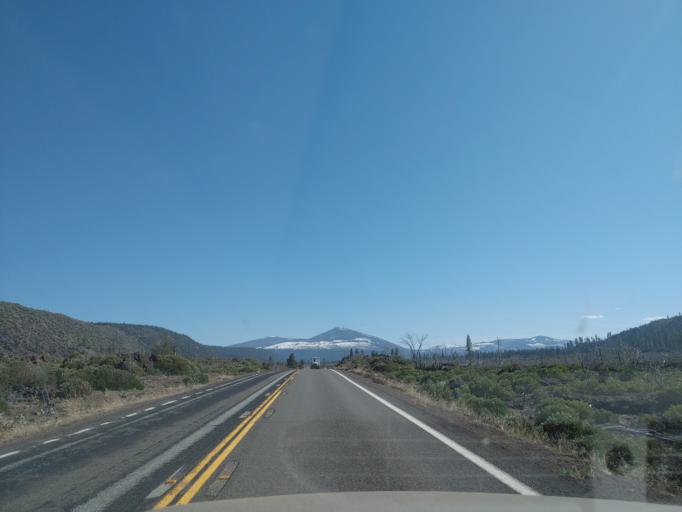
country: US
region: California
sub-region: Shasta County
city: Burney
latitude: 40.7112
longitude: -121.4212
